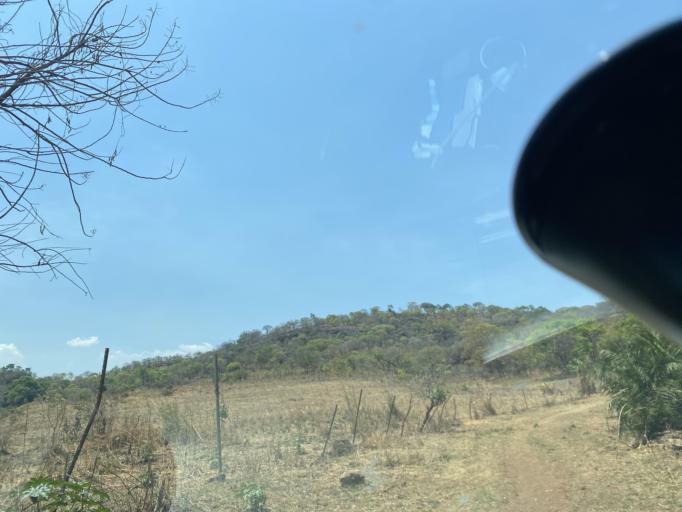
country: ZM
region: Lusaka
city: Kafue
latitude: -15.8070
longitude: 28.4336
